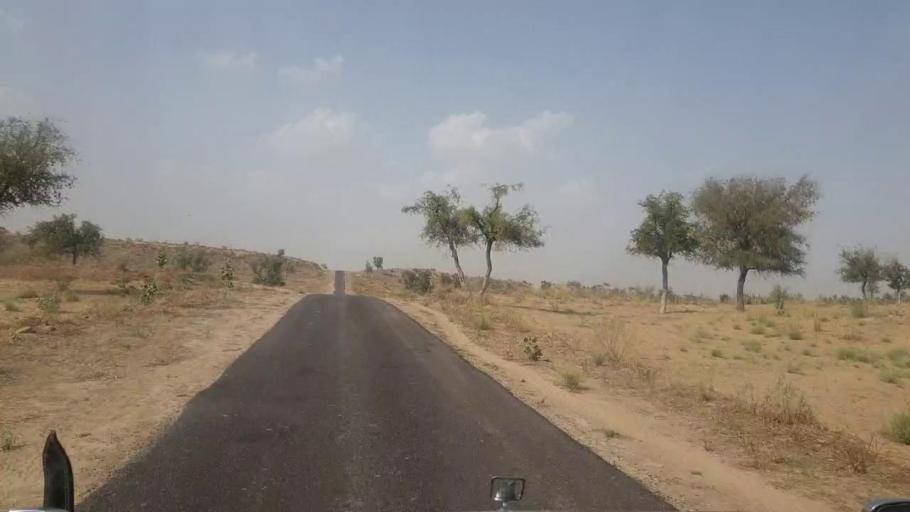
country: PK
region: Sindh
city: Islamkot
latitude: 25.1905
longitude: 70.2855
